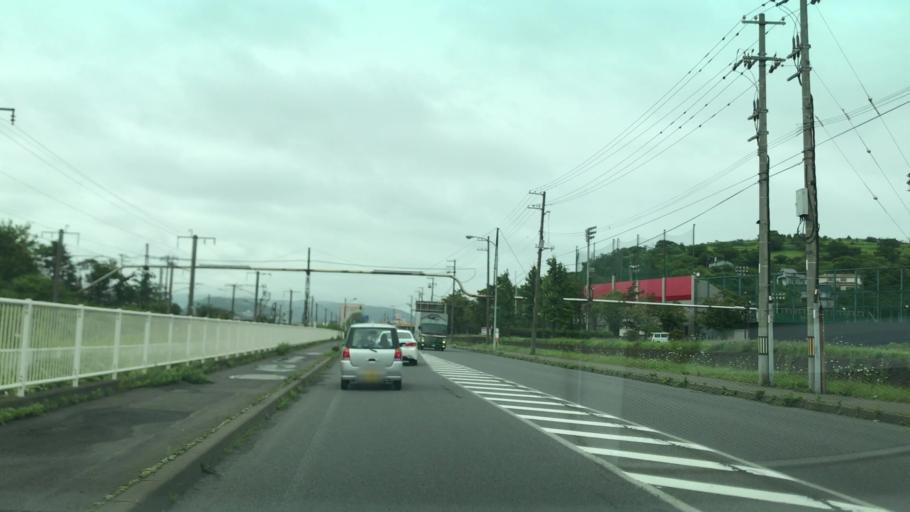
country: JP
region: Hokkaido
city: Muroran
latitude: 42.3385
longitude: 141.0148
